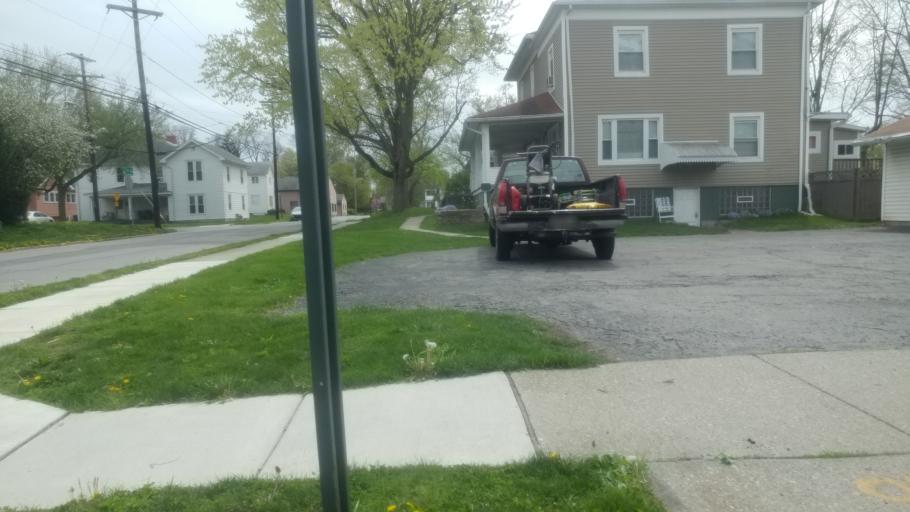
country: US
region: Ohio
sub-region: Wood County
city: Bowling Green
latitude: 41.3786
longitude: -83.6535
